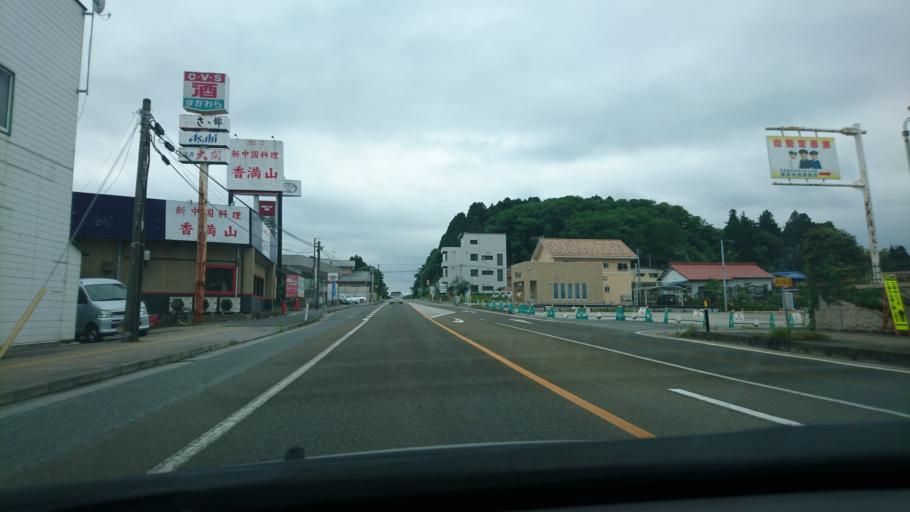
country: JP
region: Miyagi
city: Furukawa
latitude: 38.7292
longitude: 141.0221
